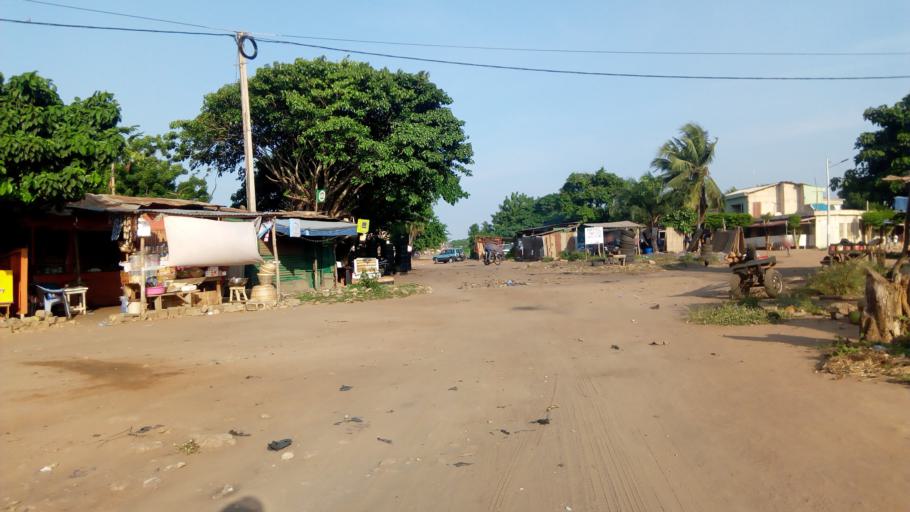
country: TG
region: Maritime
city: Lome
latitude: 6.1802
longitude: 1.1859
